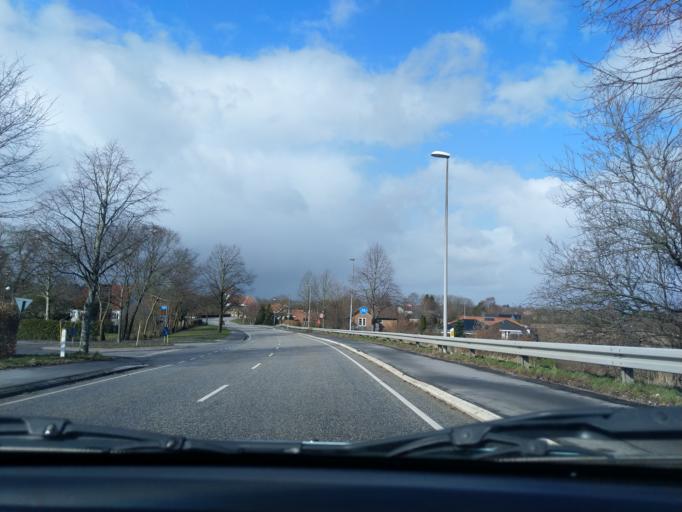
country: DK
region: Zealand
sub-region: Naestved Kommune
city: Naestved
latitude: 55.3135
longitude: 11.6831
